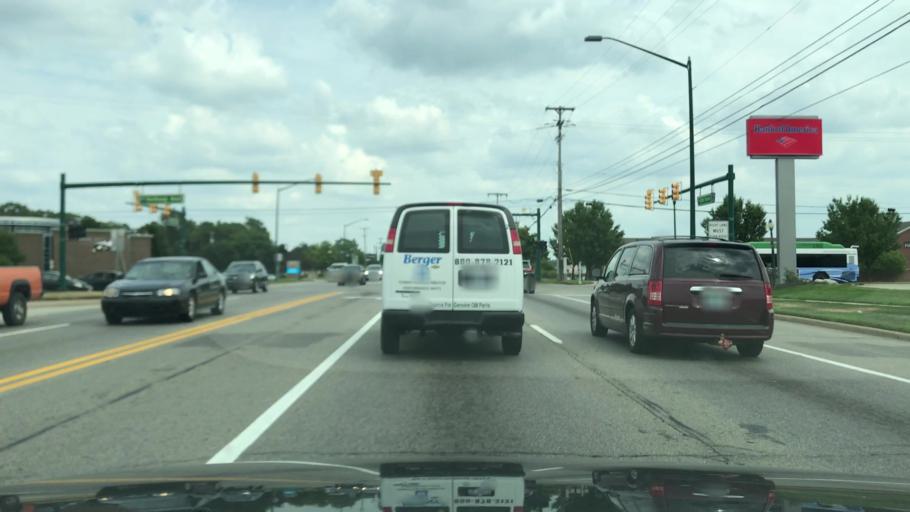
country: US
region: Michigan
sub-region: Kent County
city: Wyoming
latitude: 42.9134
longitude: -85.6962
